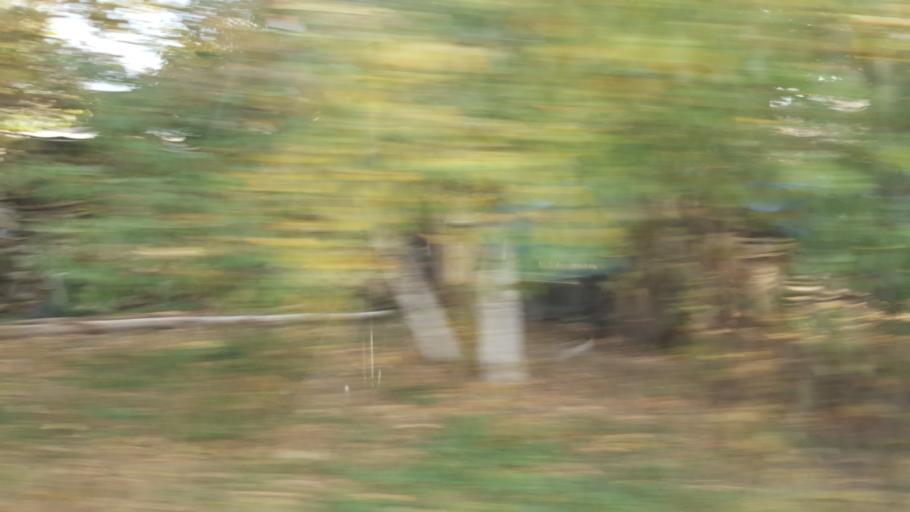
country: TR
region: Eskisehir
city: Mihaliccik
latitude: 39.9776
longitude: 31.3715
